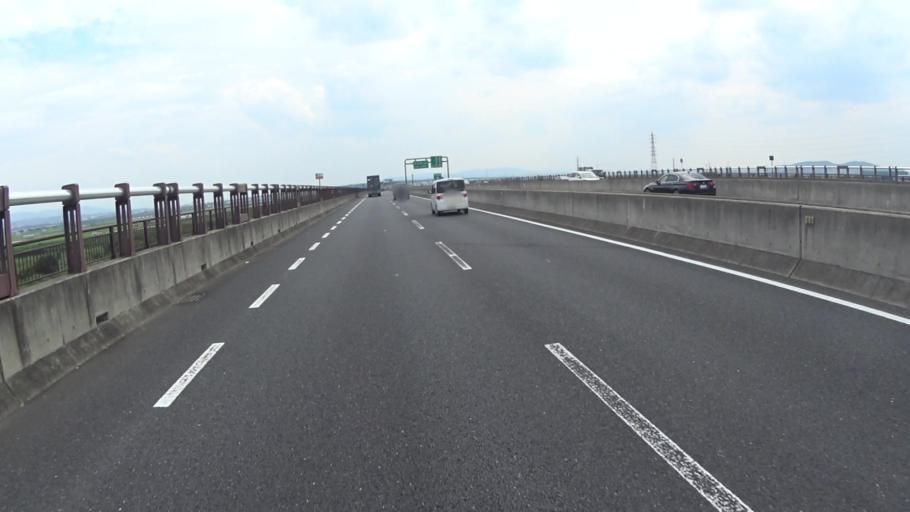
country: JP
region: Kyoto
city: Uji
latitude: 34.9181
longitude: 135.7500
